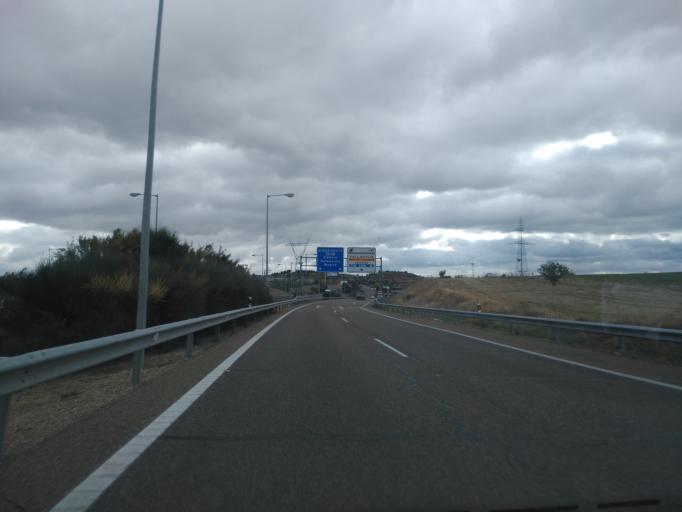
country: ES
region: Castille and Leon
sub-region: Provincia de Valladolid
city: Zaratan
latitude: 41.6659
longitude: -4.7607
